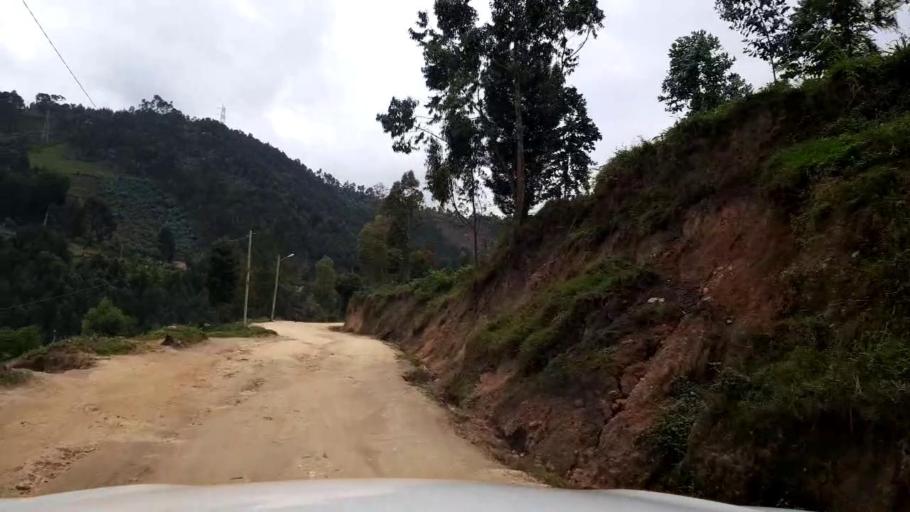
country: RW
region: Western Province
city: Kibuye
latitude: -1.9676
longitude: 29.3921
